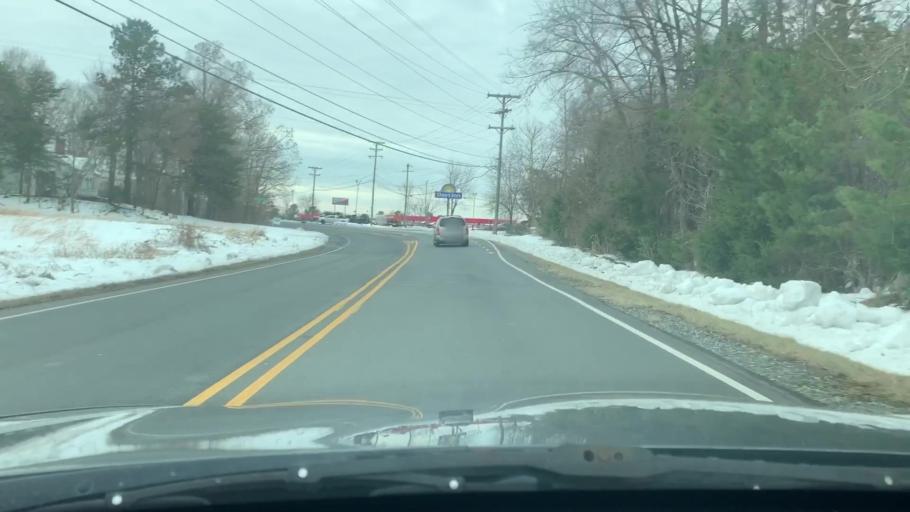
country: US
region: North Carolina
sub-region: Alamance County
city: Haw River
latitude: 36.0740
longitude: -79.3511
